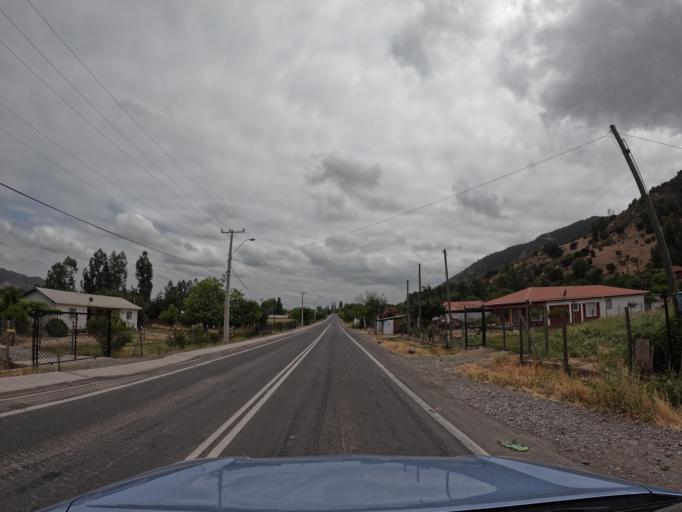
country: CL
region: Maule
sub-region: Provincia de Curico
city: Teno
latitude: -34.7859
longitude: -71.2292
